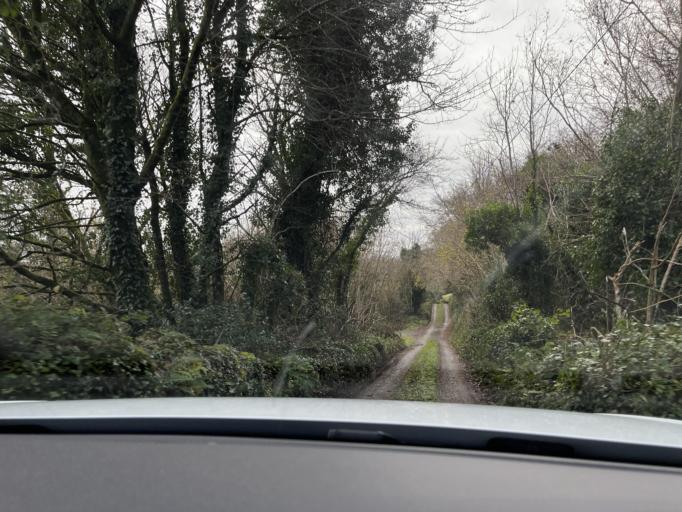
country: IE
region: Connaught
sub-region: Sligo
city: Sligo
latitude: 54.2668
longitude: -8.3526
